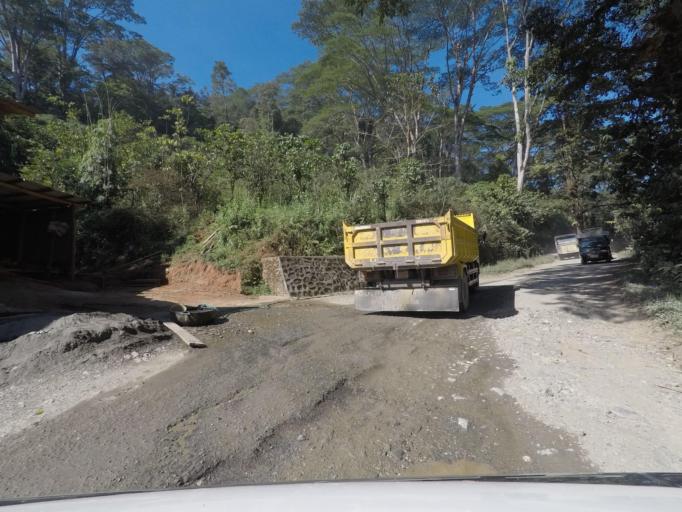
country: TL
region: Ermera
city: Gleno
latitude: -8.7335
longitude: 125.4347
